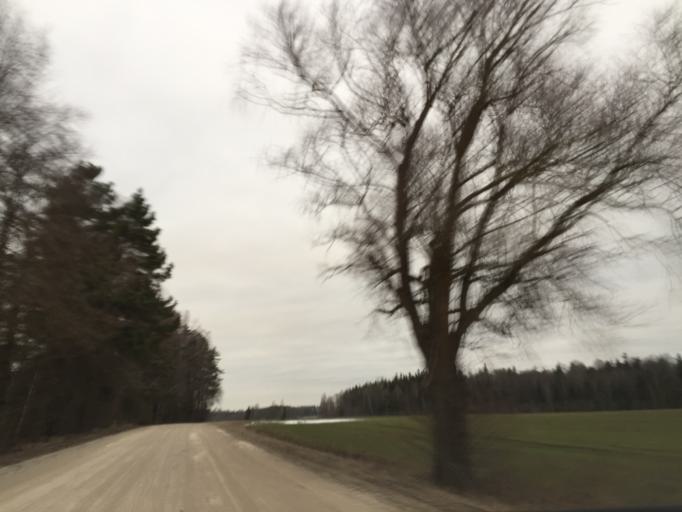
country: LT
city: Zagare
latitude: 56.2838
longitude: 23.2588
